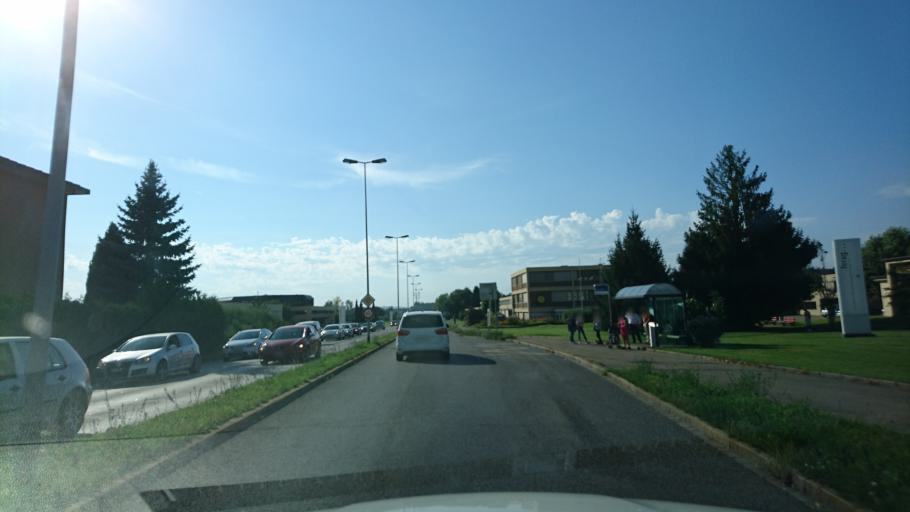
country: CH
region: Zurich
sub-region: Bezirk Hinwil
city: Hinwil
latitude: 47.3039
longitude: 8.8328
